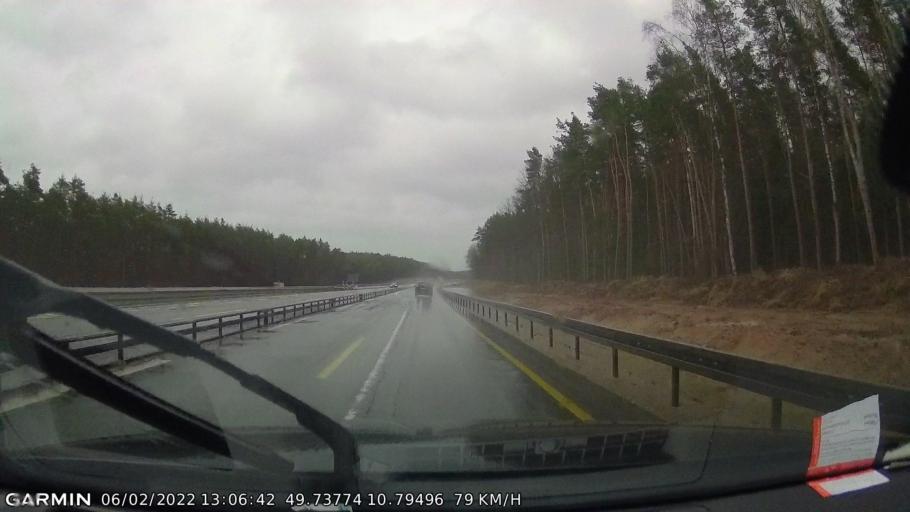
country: DE
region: Bavaria
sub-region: Regierungsbezirk Mittelfranken
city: Muhlhausen
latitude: 49.7376
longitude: 10.7948
